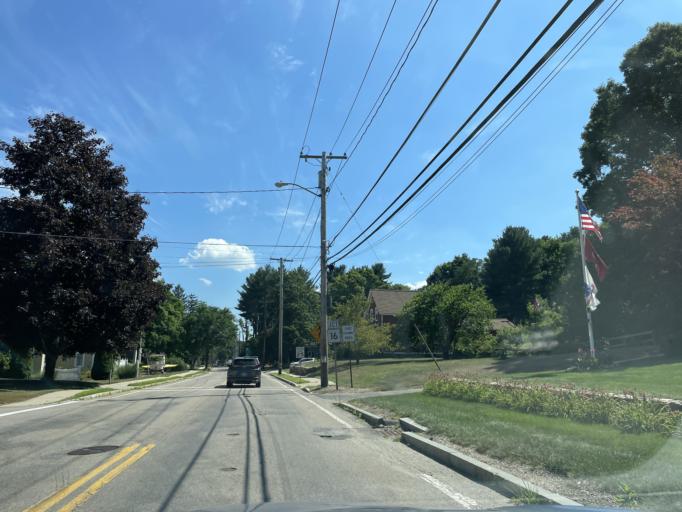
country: US
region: Massachusetts
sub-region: Middlesex County
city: Holliston
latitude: 42.2143
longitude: -71.4256
